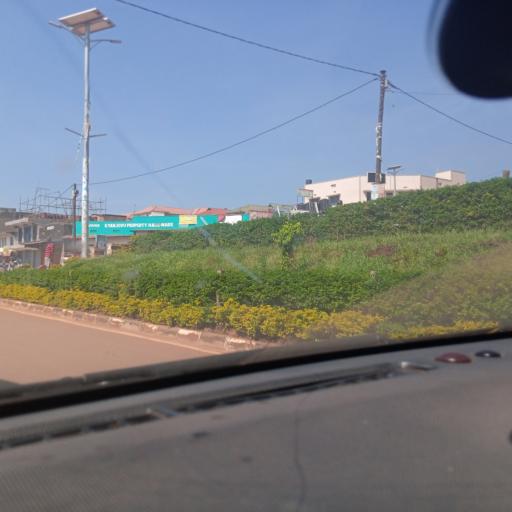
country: UG
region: Central Region
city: Masaka
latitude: -0.3431
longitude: 31.7399
